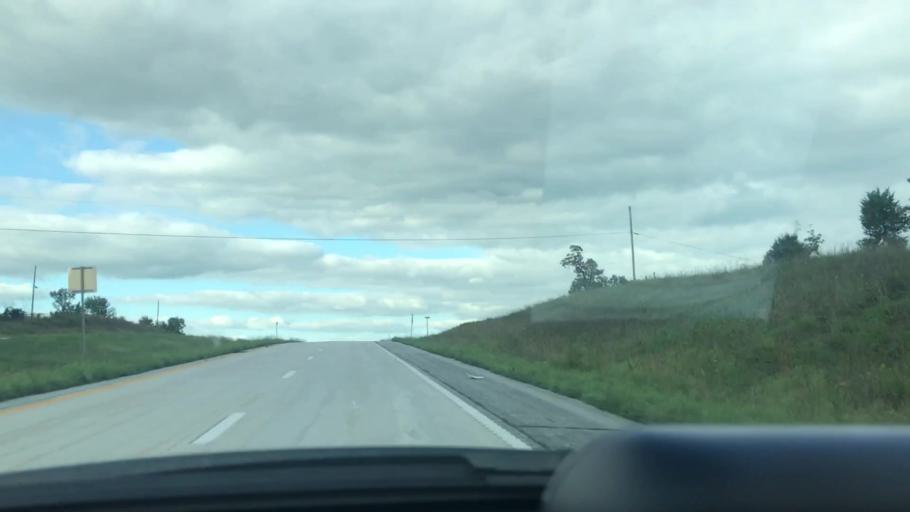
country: US
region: Missouri
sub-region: Benton County
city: Lincoln
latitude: 38.4403
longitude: -93.2977
